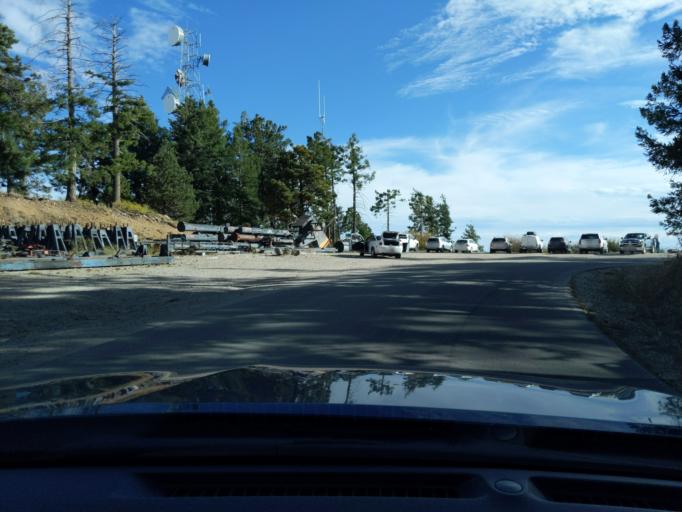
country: US
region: Arizona
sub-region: Pima County
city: Catalina
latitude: 32.4413
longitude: -110.7840
